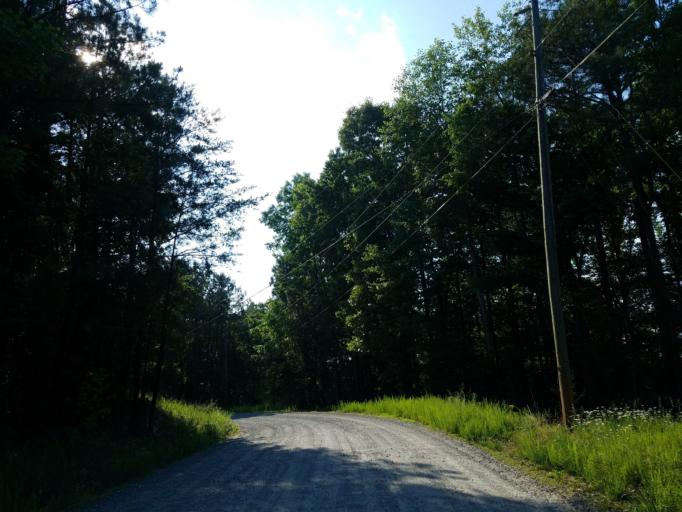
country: US
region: Georgia
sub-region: Pickens County
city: Nelson
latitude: 34.3720
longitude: -84.3398
